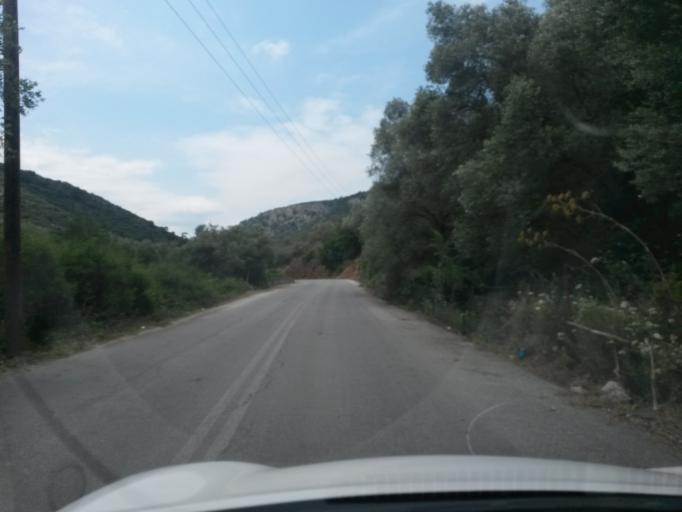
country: GR
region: North Aegean
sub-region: Nomos Lesvou
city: Pamfylla
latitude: 39.1903
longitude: 26.4446
